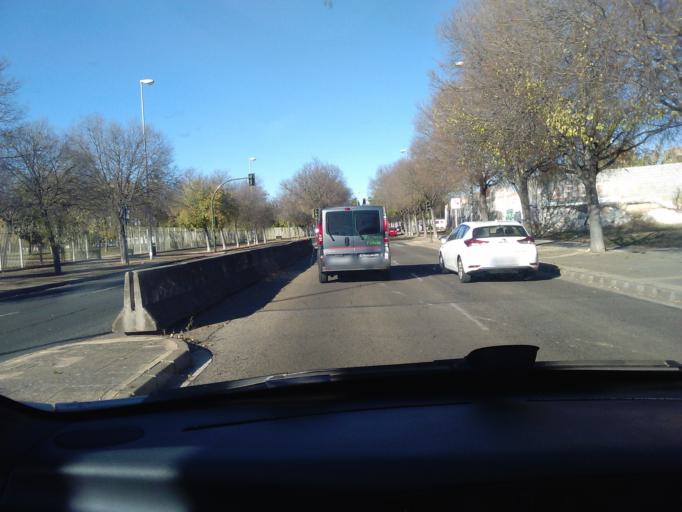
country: ES
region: Andalusia
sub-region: Provincia de Sevilla
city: Sevilla
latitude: 37.4242
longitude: -5.9878
